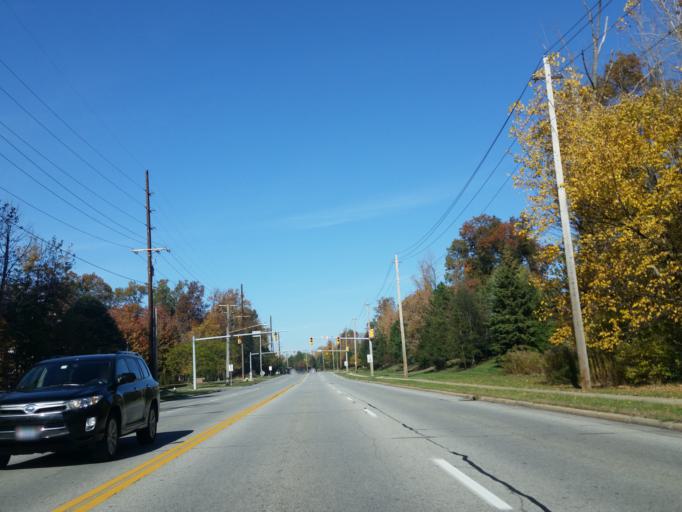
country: US
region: Ohio
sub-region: Cuyahoga County
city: Westlake
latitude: 41.4412
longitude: -81.9474
